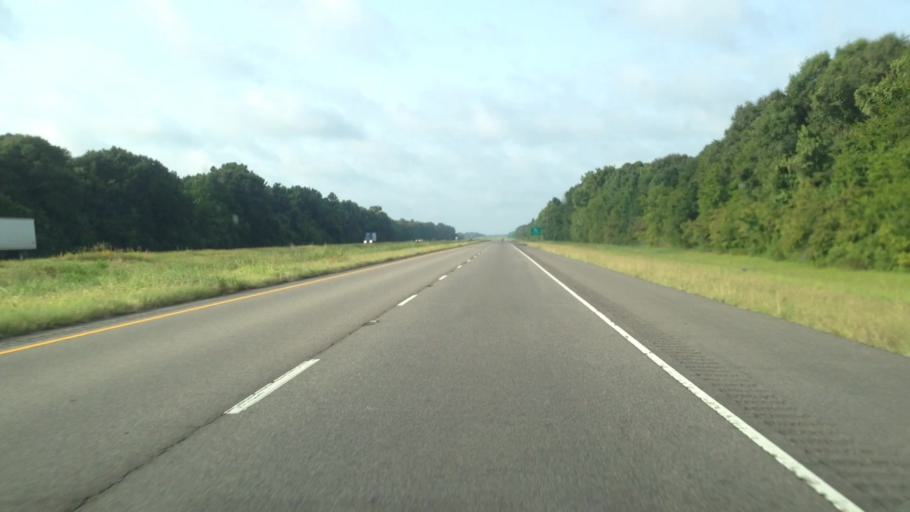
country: US
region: Louisiana
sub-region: Avoyelles Parish
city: Bunkie
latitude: 30.8897
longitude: -92.2272
